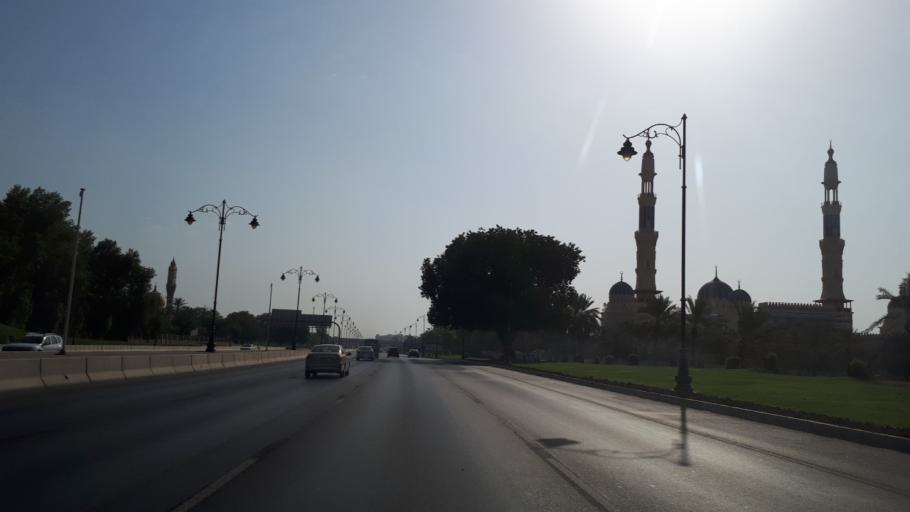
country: OM
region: Muhafazat Masqat
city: Bawshar
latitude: 23.6145
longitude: 58.4790
